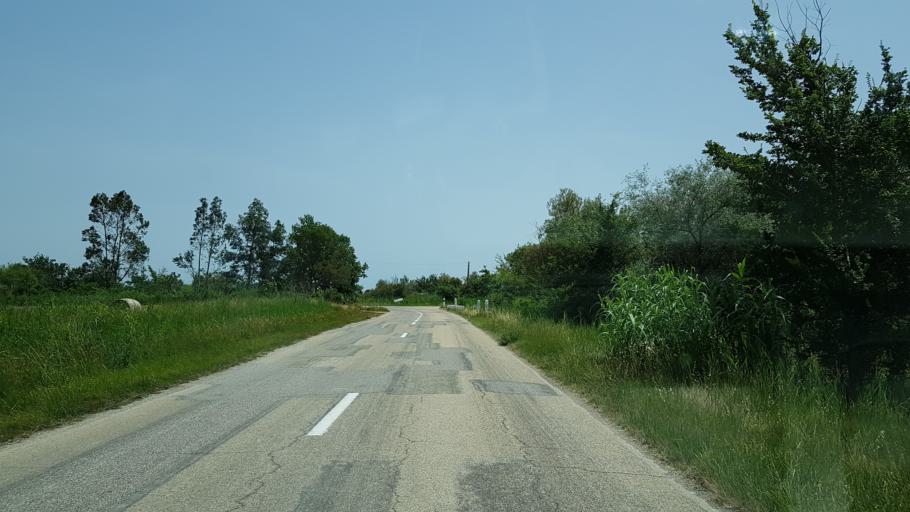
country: FR
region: Provence-Alpes-Cote d'Azur
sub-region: Departement des Bouches-du-Rhone
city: Port-Saint-Louis-du-Rhone
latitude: 43.4294
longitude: 4.6932
